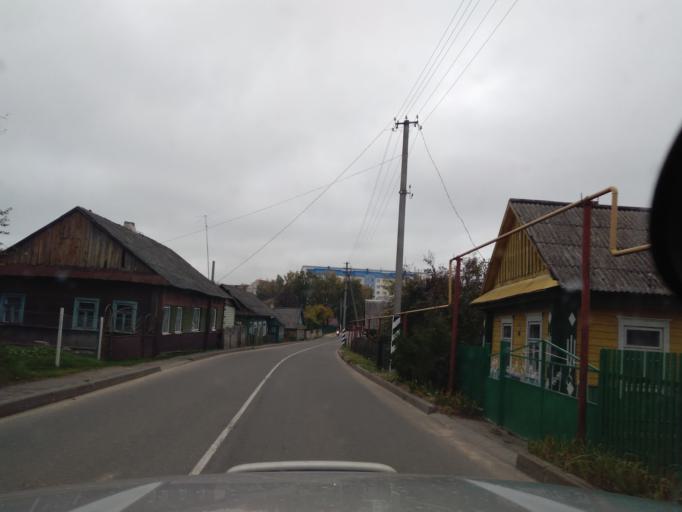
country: BY
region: Minsk
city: Kapyl'
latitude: 53.1462
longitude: 27.0923
